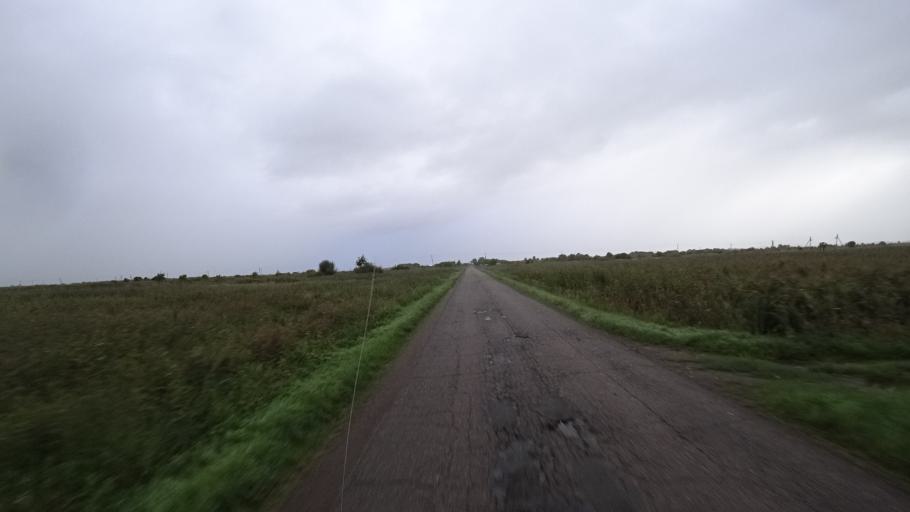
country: RU
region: Primorskiy
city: Chernigovka
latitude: 44.3923
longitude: 132.5288
